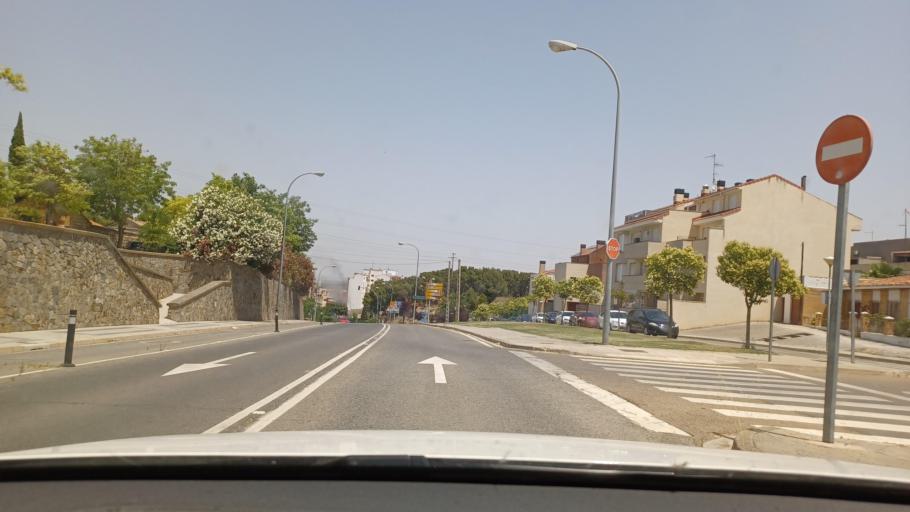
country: ES
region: Navarre
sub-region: Provincia de Navarra
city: Tudela
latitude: 42.0560
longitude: -1.6094
